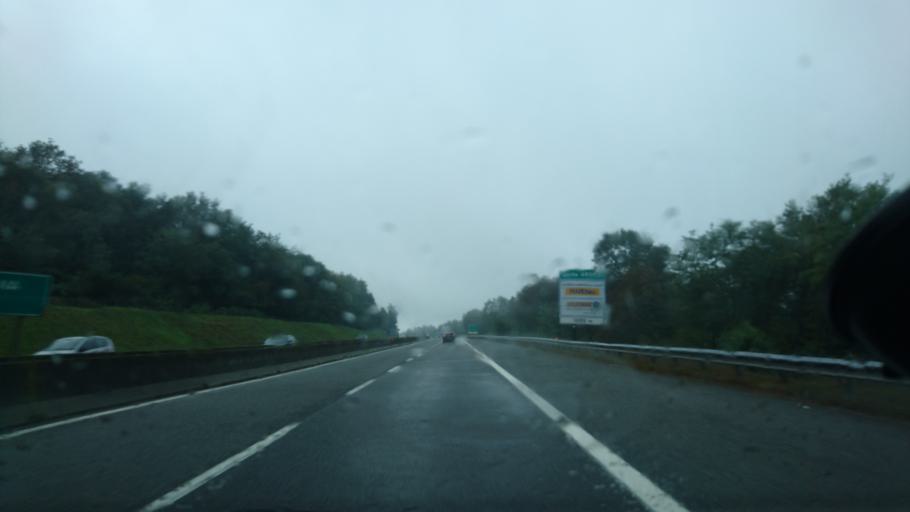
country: IT
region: Piedmont
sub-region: Provincia di Novara
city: Gattico
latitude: 45.7230
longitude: 8.5225
